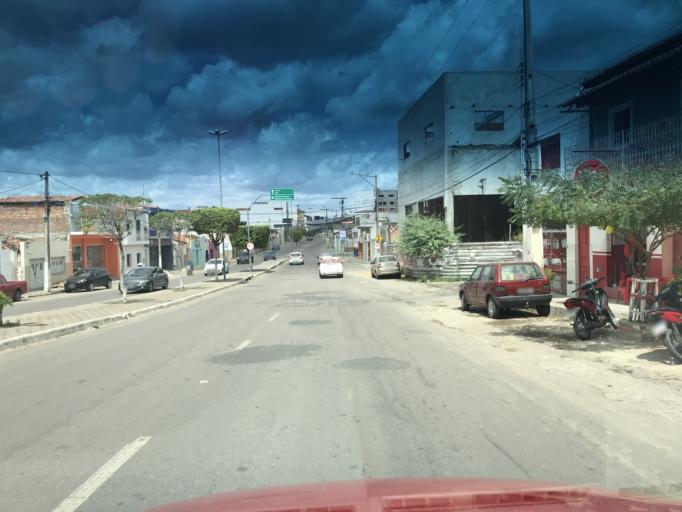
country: BR
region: Bahia
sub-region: Itaberaba
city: Itaberaba
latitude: -12.5273
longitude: -40.3071
